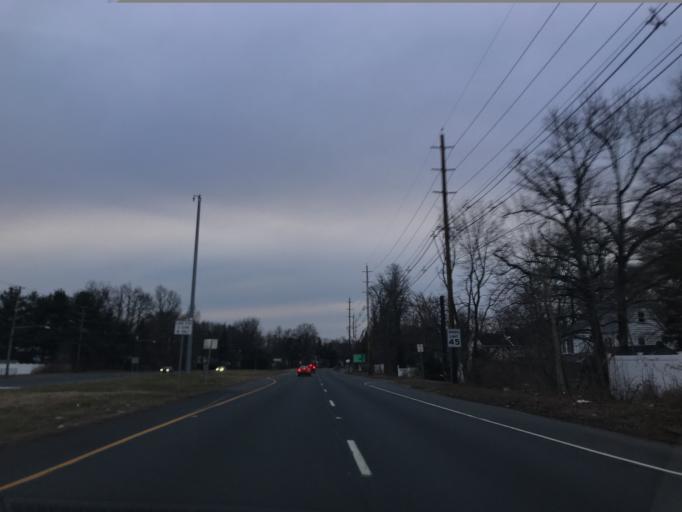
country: US
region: New Jersey
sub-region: Middlesex County
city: Milltown
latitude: 40.4542
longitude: -74.4581
